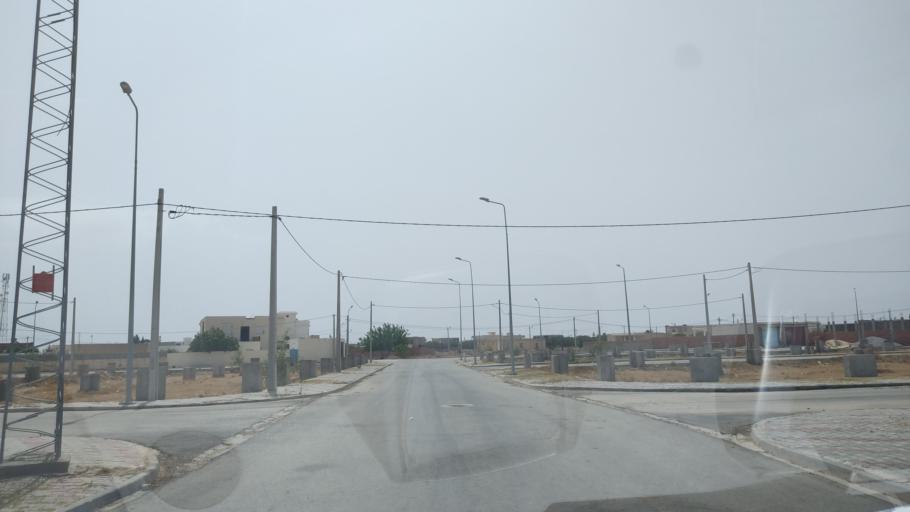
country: TN
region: Al Mahdiyah
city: El Jem
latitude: 35.1276
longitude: 10.7359
